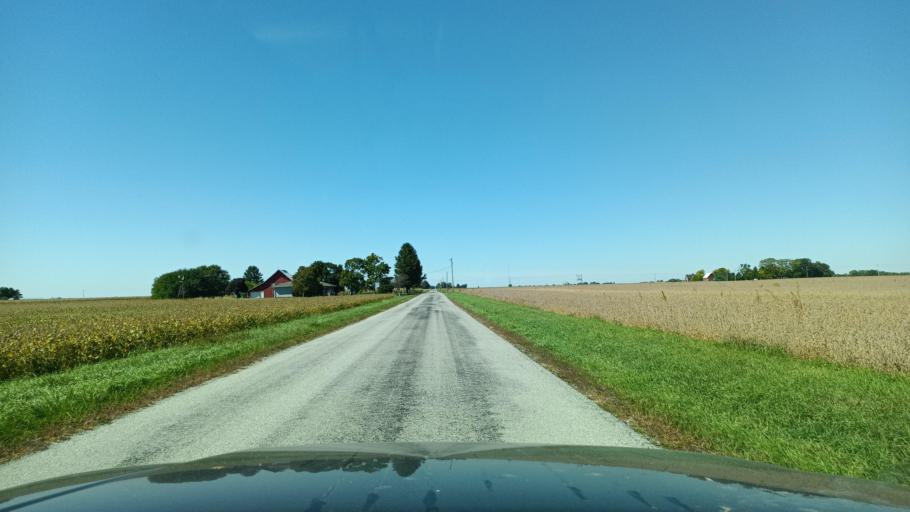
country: US
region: Illinois
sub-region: Champaign County
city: Mahomet
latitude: 40.0988
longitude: -88.3614
